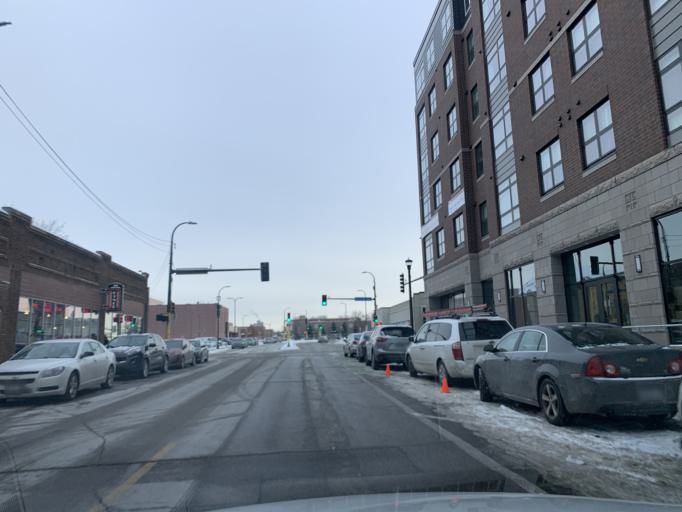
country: US
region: Minnesota
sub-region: Hennepin County
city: Minneapolis
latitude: 44.9677
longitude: -93.2785
